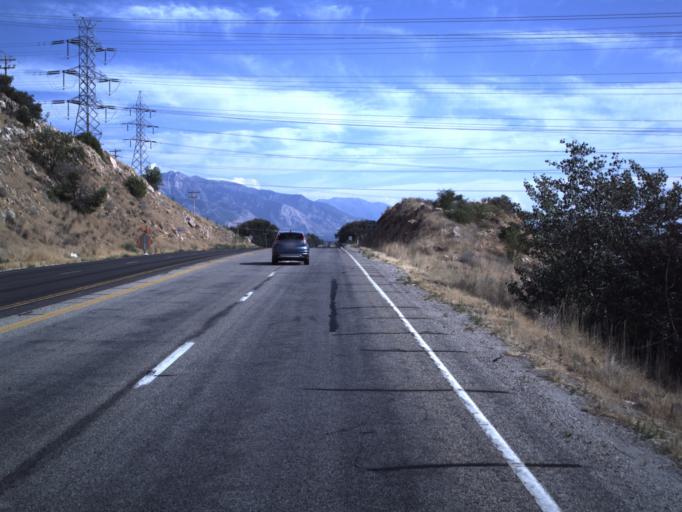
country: US
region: Utah
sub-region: Box Elder County
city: South Willard
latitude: 41.3385
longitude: -112.0298
